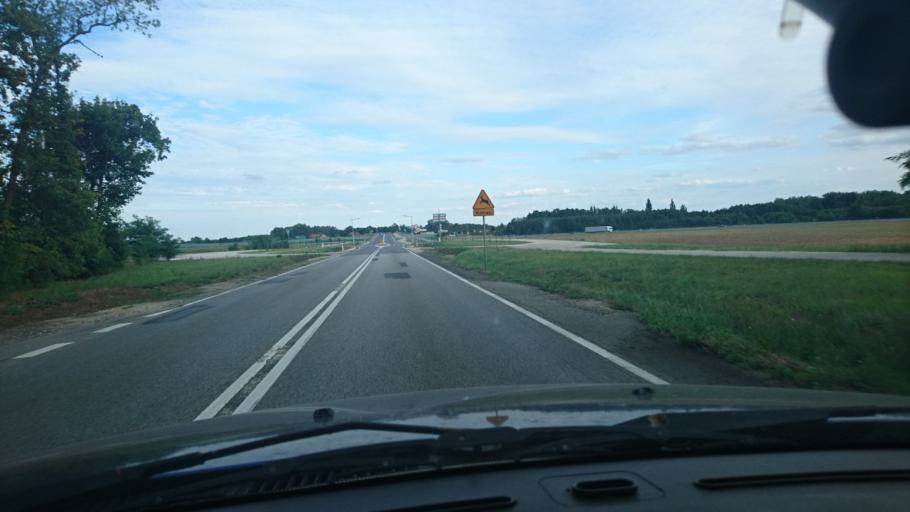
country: PL
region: Greater Poland Voivodeship
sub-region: Powiat kepinski
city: Kepno
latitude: 51.3203
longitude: 17.9740
